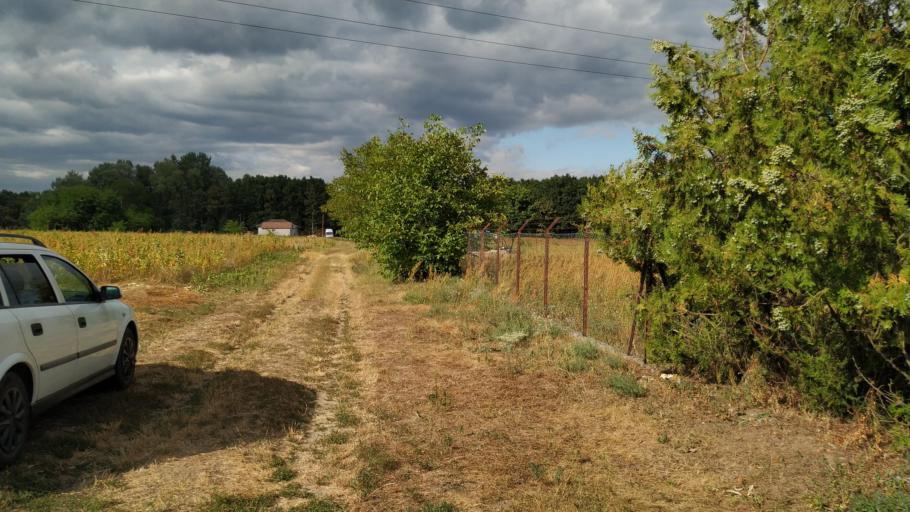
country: HU
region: Pest
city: Nagykata
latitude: 47.3992
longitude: 19.7425
